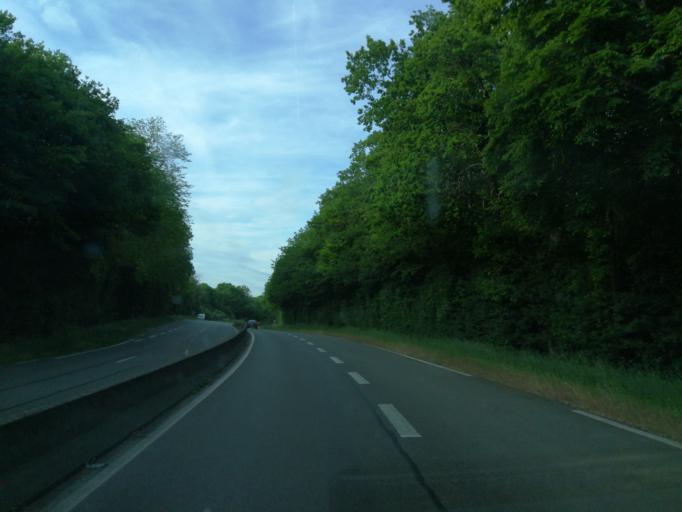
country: FR
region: Centre
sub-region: Departement d'Eure-et-Loir
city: Gallardon
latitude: 48.4997
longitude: 1.7110
